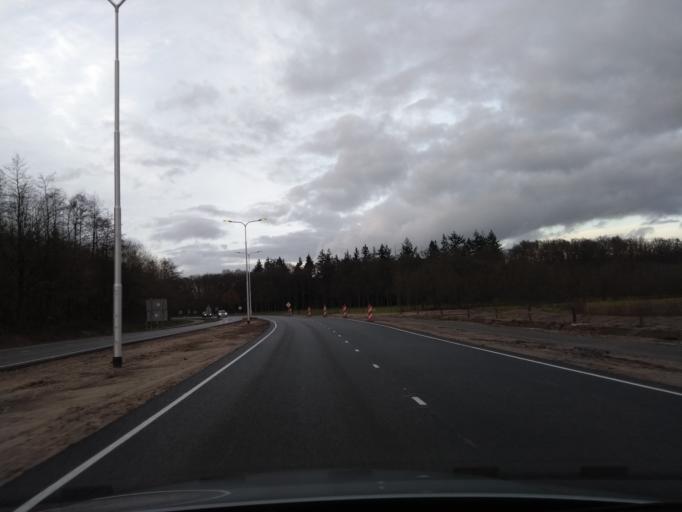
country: NL
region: Overijssel
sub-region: Gemeente Enschede
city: Enschede
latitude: 52.2762
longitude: 6.8685
